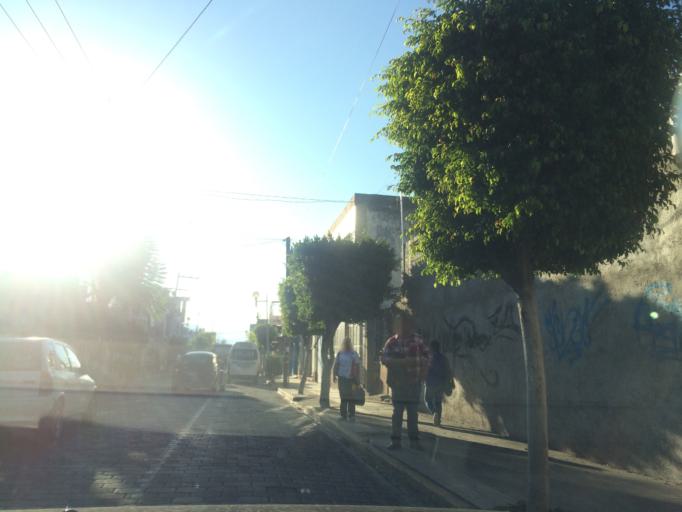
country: MX
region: Puebla
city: Tehuacan
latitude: 18.4632
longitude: -97.4001
